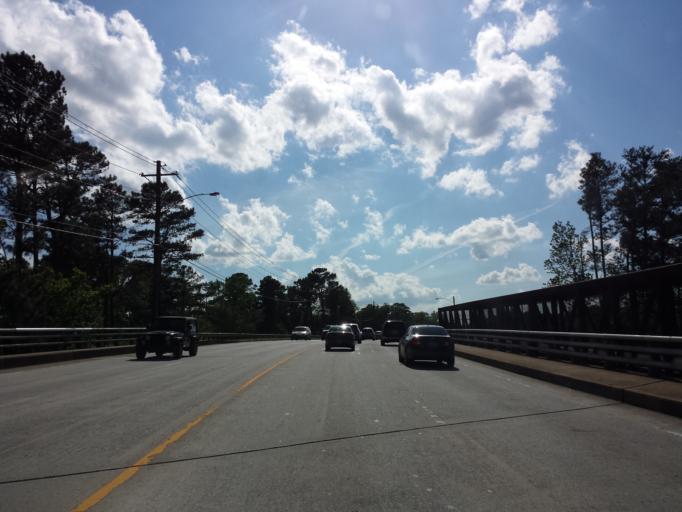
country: US
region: Georgia
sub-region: Cobb County
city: Smyrna
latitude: 33.8805
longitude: -84.5086
